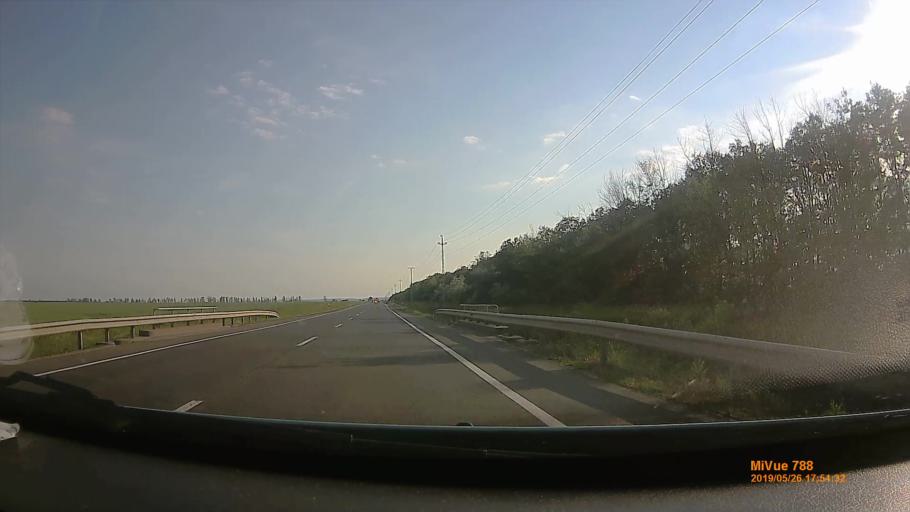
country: HU
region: Borsod-Abauj-Zemplen
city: Arnot
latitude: 48.1399
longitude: 20.8847
